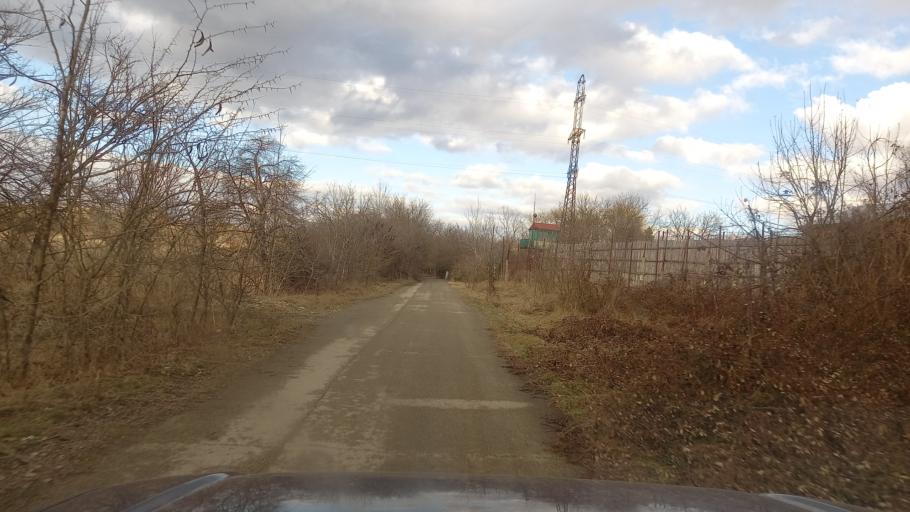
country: RU
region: Adygeya
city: Maykop
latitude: 44.5917
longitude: 40.0743
